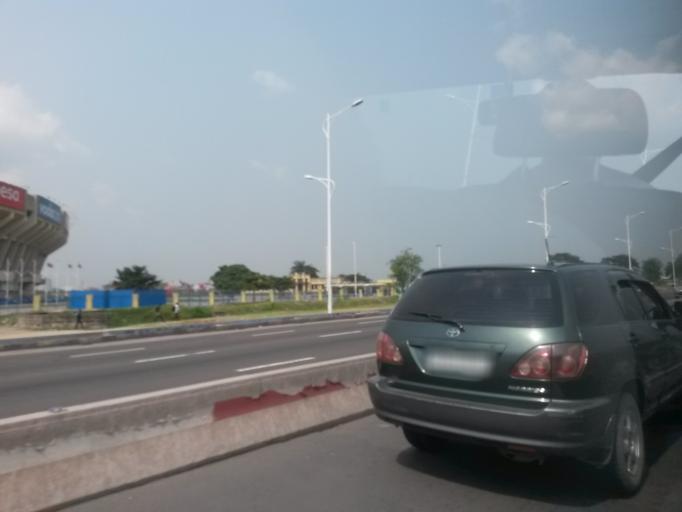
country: CD
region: Kinshasa
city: Kinshasa
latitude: -4.3327
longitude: 15.3110
